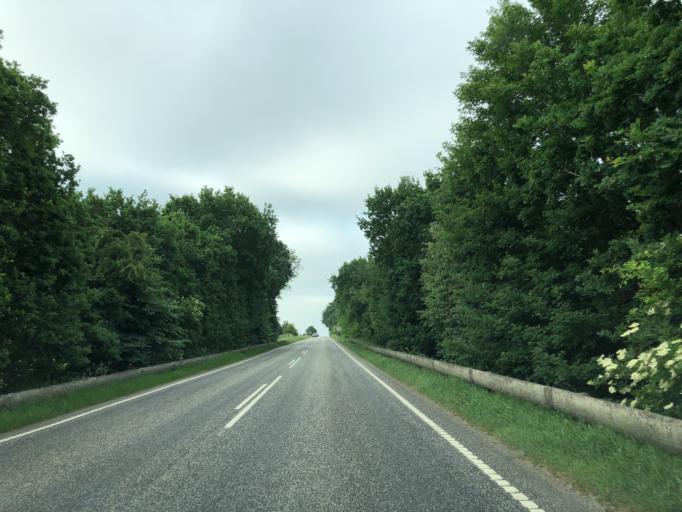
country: DK
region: South Denmark
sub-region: Vejle Kommune
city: Give
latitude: 55.8522
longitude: 9.2479
